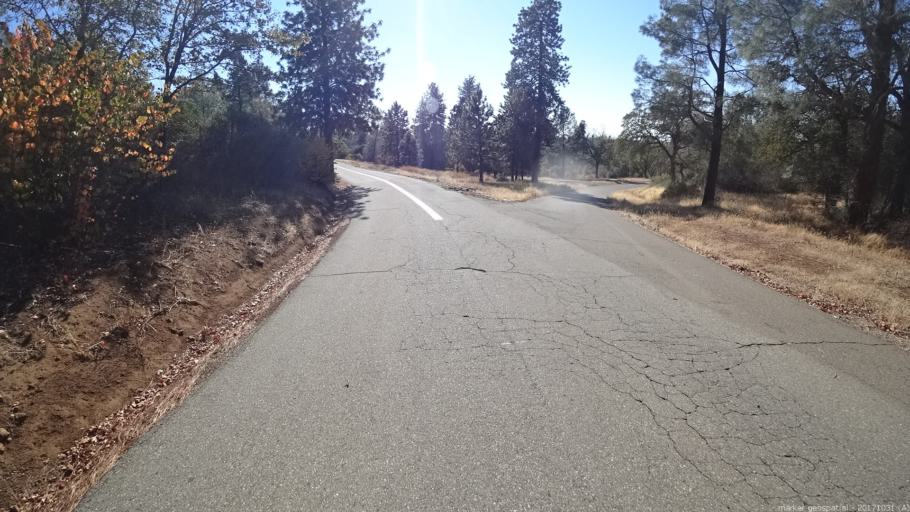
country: US
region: California
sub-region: Shasta County
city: Shingletown
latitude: 40.4578
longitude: -122.0059
